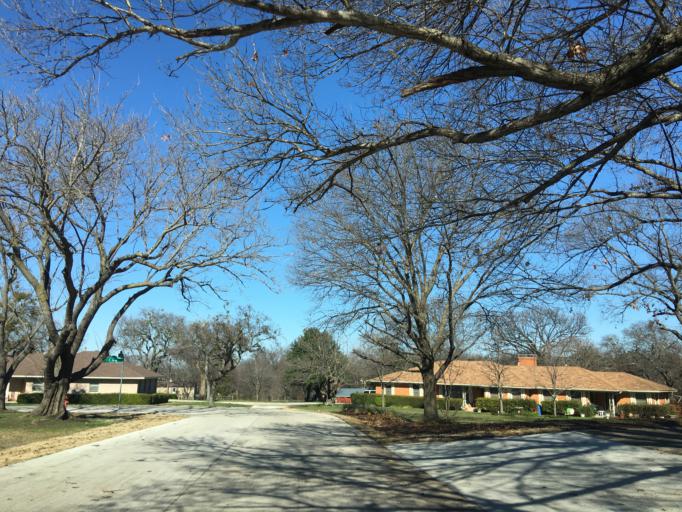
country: US
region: Texas
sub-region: Collin County
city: Prosper
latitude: 33.2346
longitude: -96.7948
